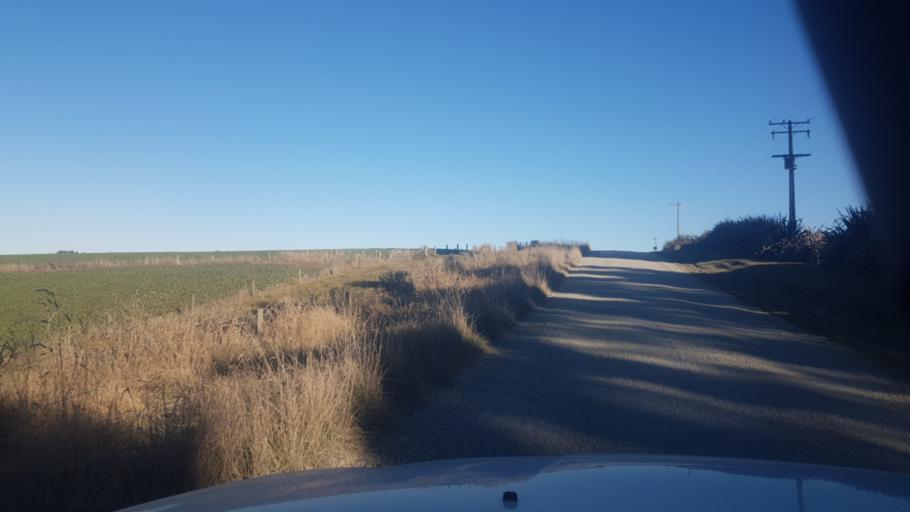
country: NZ
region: Canterbury
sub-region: Timaru District
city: Pleasant Point
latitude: -44.3499
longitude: 171.0726
